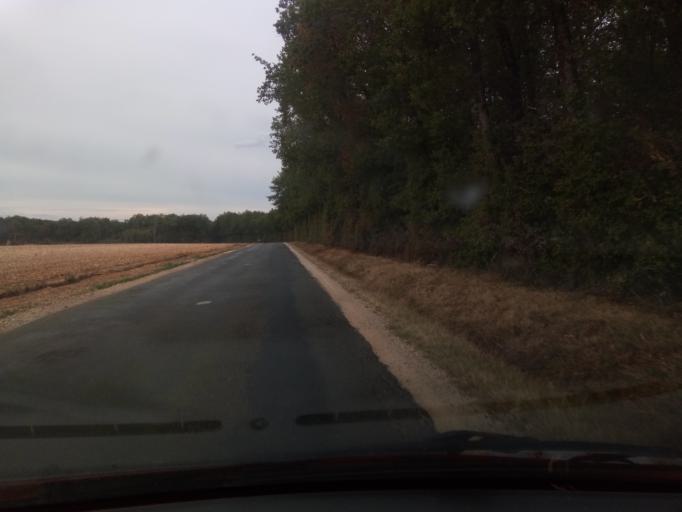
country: FR
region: Poitou-Charentes
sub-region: Departement de la Vienne
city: Saint-Savin
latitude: 46.5322
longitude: 0.7789
